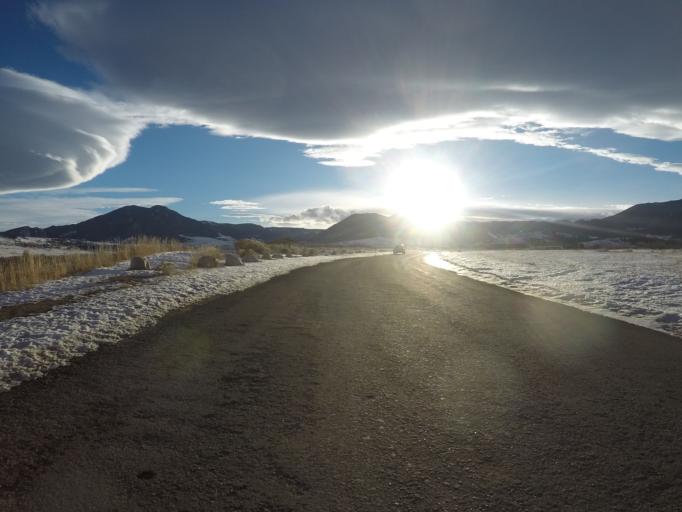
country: US
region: Montana
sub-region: Carbon County
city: Red Lodge
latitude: 45.1848
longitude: -109.2537
